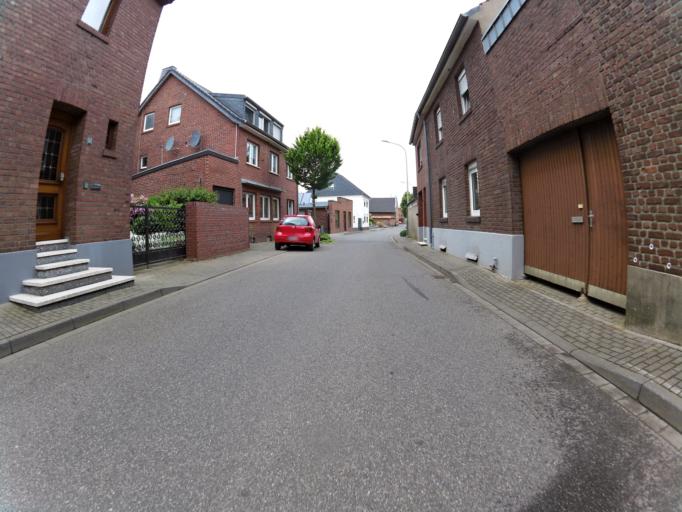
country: DE
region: North Rhine-Westphalia
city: Geilenkirchen
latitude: 50.9849
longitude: 6.1848
